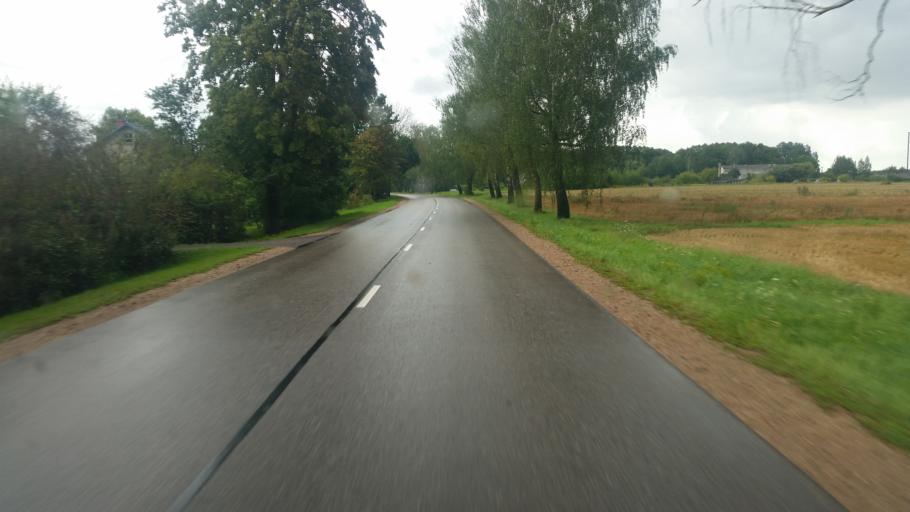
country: LV
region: Bauskas Rajons
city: Bauska
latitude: 56.4296
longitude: 24.3257
